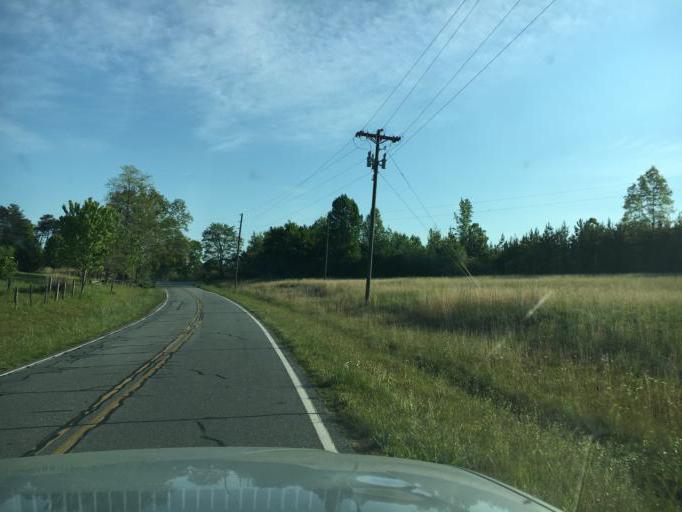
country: US
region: North Carolina
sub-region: Rutherford County
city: Rutherfordton
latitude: 35.3172
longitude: -81.9912
